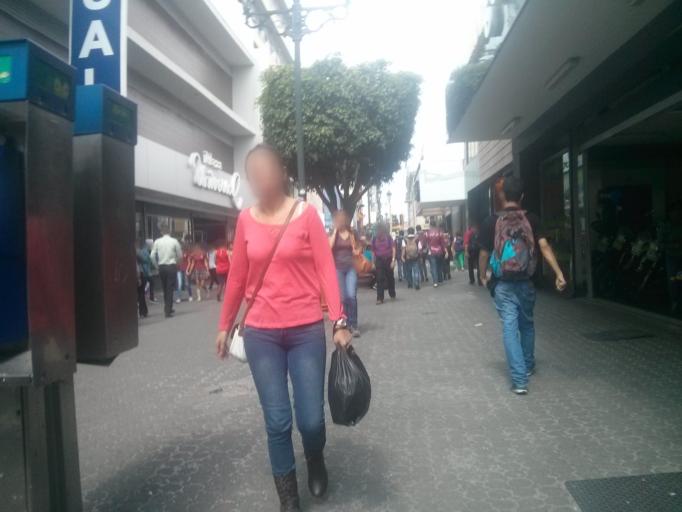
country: CR
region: San Jose
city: San Jose
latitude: 9.9339
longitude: -84.0791
